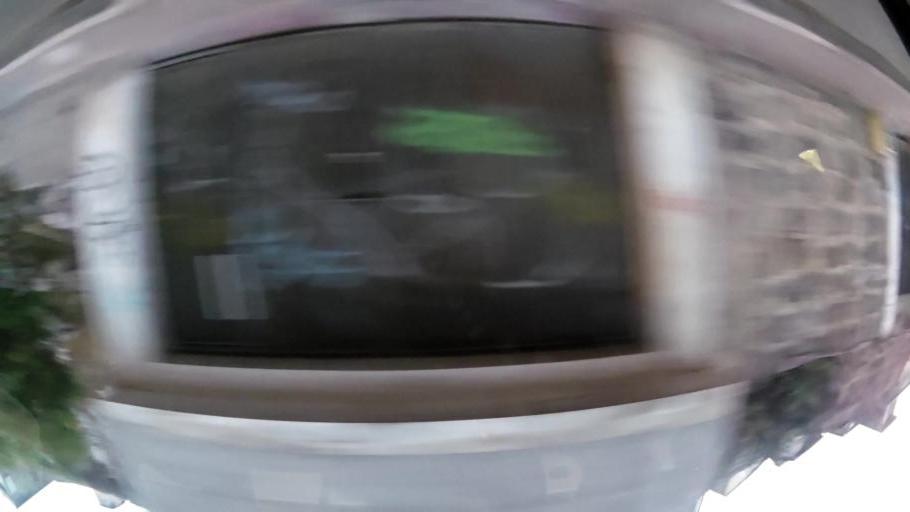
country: EC
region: Tungurahua
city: Ambato
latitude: -1.2456
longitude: -78.6337
